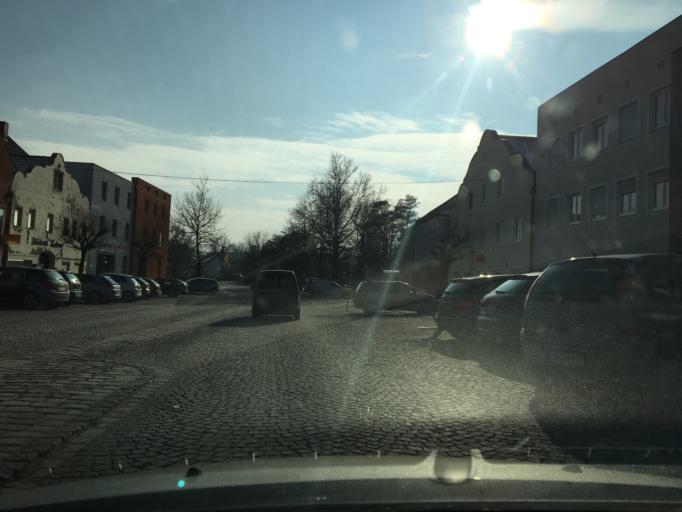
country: DE
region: Bavaria
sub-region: Lower Bavaria
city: Gangkofen
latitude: 48.4369
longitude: 12.5633
